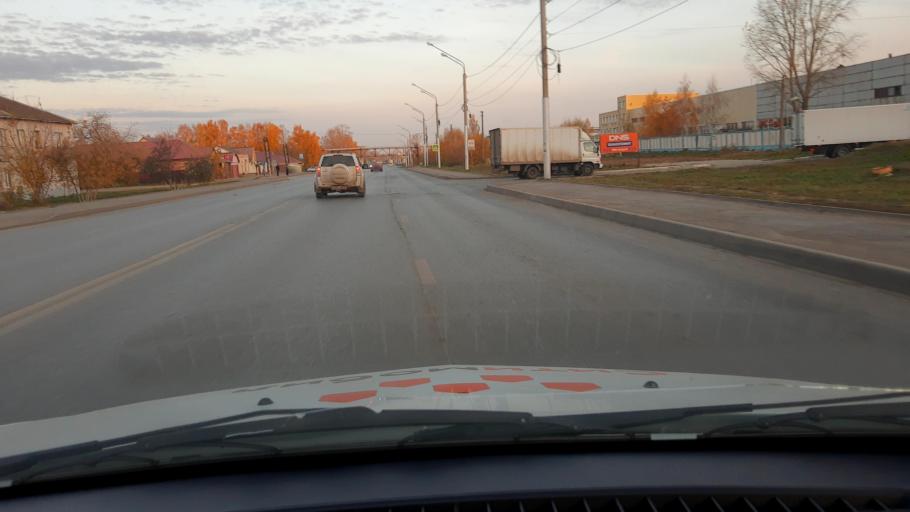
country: RU
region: Bashkortostan
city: Iglino
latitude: 54.7607
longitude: 56.2433
